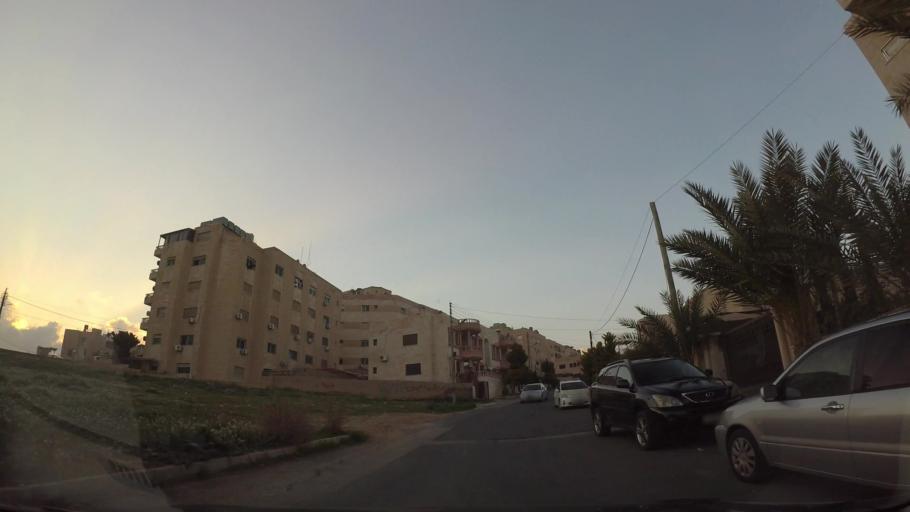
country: JO
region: Amman
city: Amman
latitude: 31.9951
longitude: 35.9486
